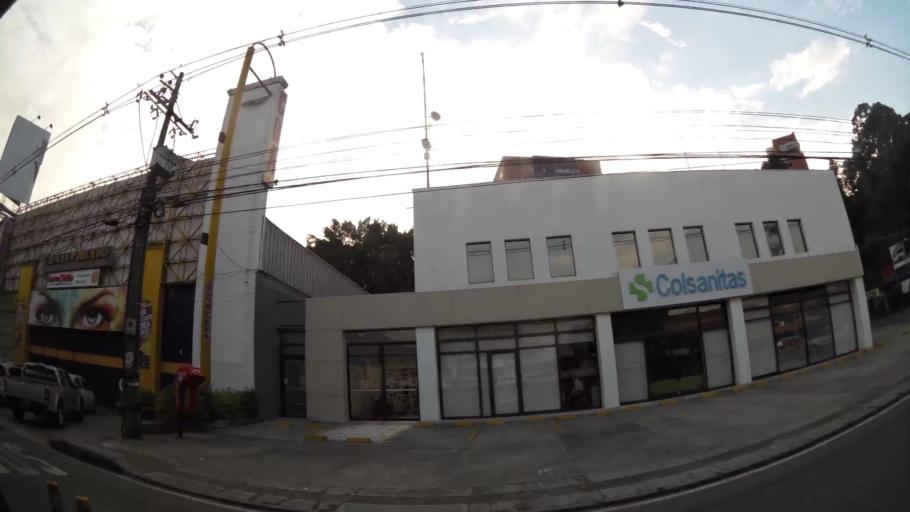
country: CO
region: Antioquia
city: Medellin
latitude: 6.2251
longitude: -75.5692
